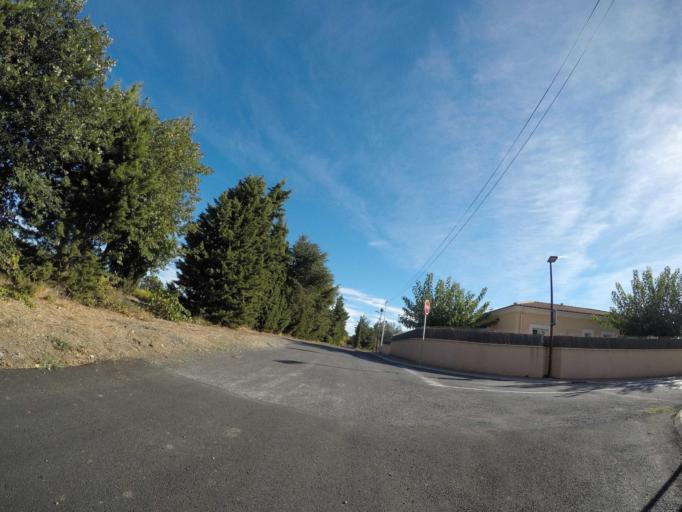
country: FR
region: Languedoc-Roussillon
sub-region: Departement des Pyrenees-Orientales
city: Villemolaque
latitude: 42.5772
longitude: 2.8082
